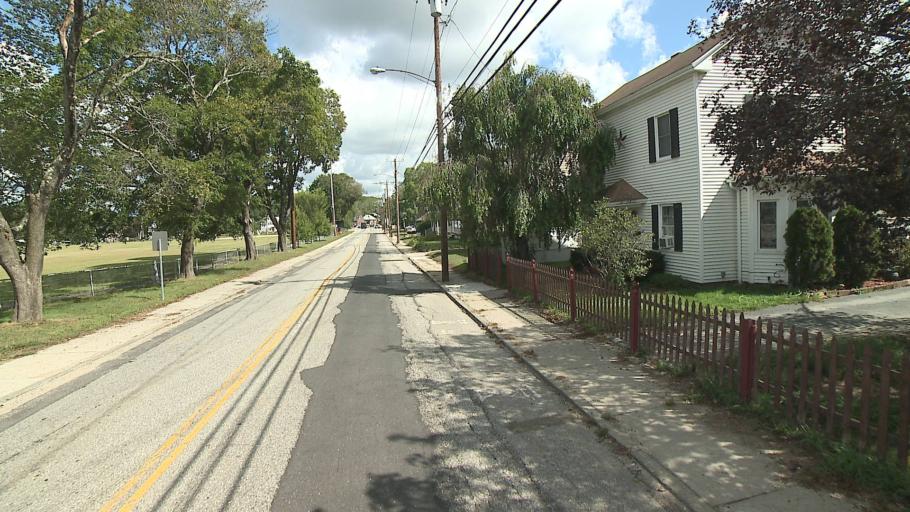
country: US
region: Connecticut
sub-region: Windham County
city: Putnam
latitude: 41.9194
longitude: -71.9036
